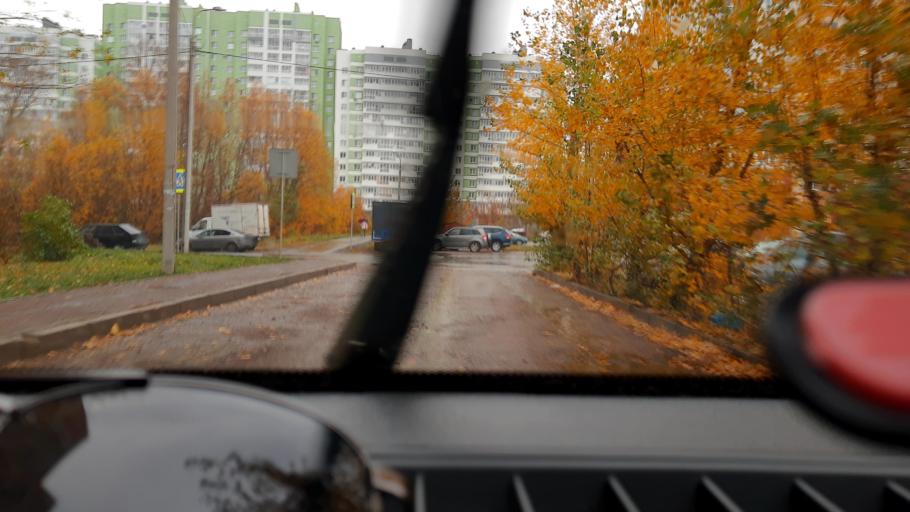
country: RU
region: Bashkortostan
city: Ufa
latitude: 54.7842
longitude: 56.1128
